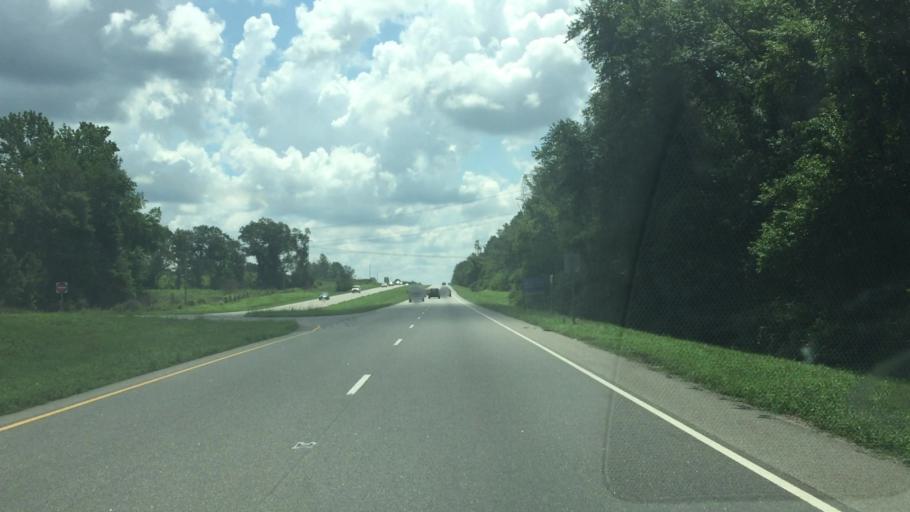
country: US
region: North Carolina
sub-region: Richmond County
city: Hamlet
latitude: 34.8540
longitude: -79.6227
